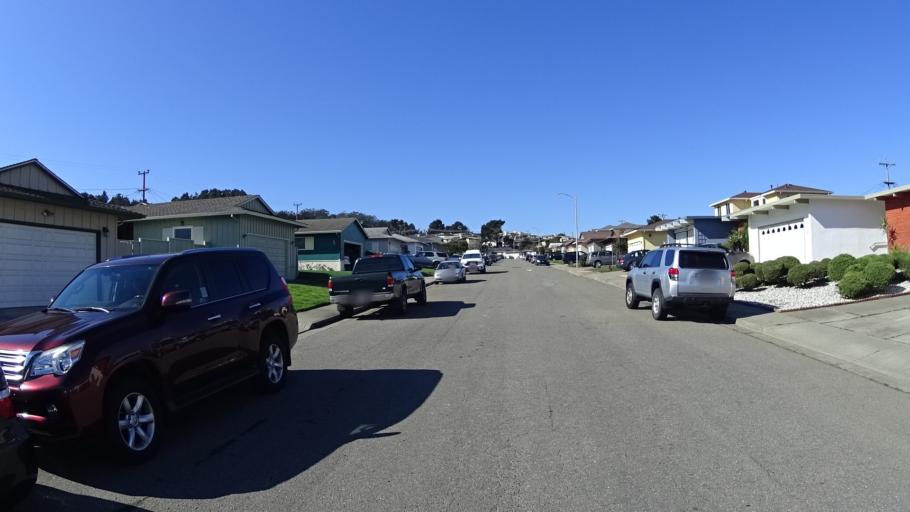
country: US
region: California
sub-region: San Mateo County
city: Colma
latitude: 37.6392
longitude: -122.4570
